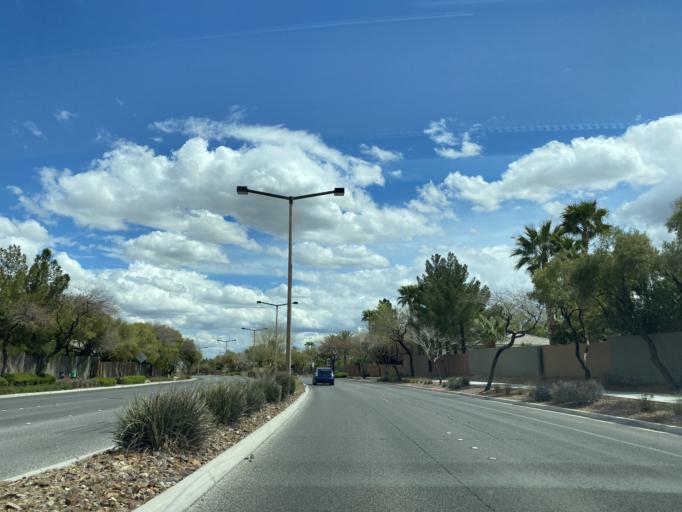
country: US
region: Nevada
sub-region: Clark County
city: Summerlin South
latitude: 36.1671
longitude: -115.3205
